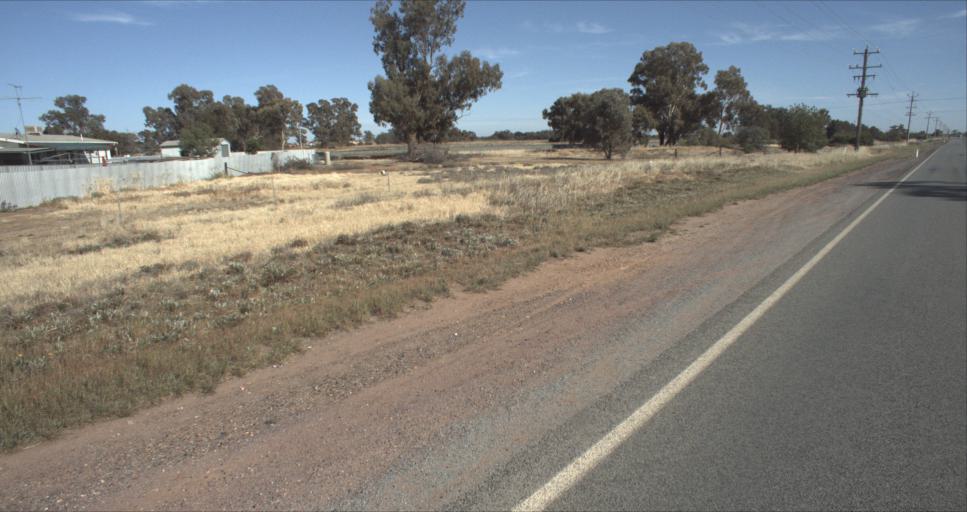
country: AU
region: New South Wales
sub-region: Leeton
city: Leeton
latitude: -34.5970
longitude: 146.4056
